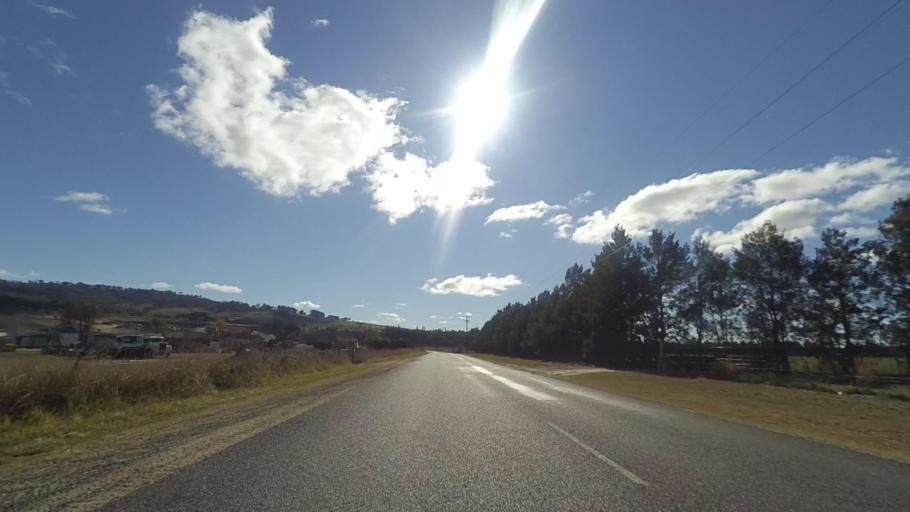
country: AU
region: New South Wales
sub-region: Bathurst Regional
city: Perthville
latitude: -33.4694
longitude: 149.5744
